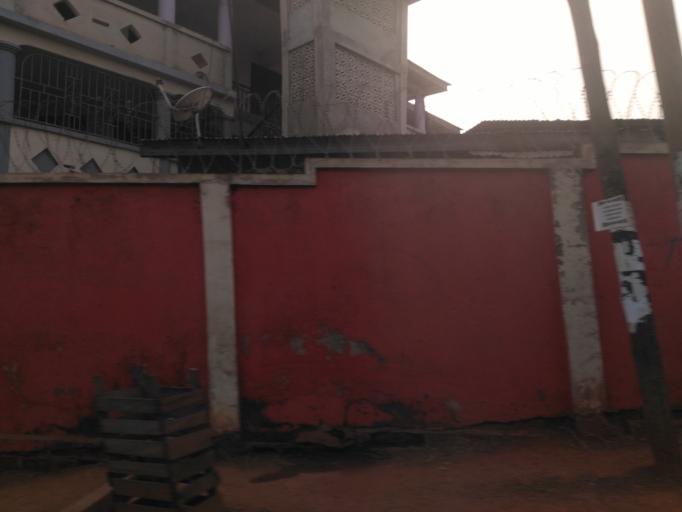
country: GH
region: Ashanti
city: Tafo
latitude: 6.7100
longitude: -1.6094
